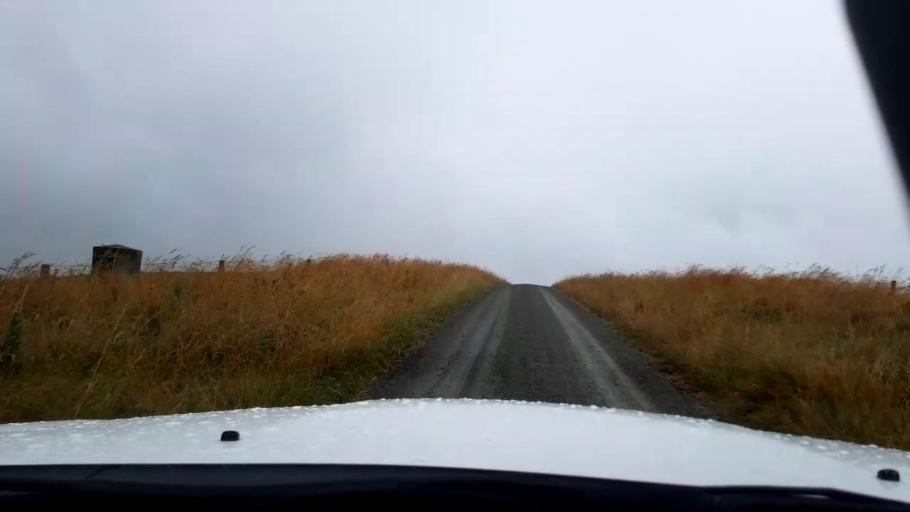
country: NZ
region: Canterbury
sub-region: Timaru District
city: Pleasant Point
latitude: -44.1753
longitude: 171.0915
